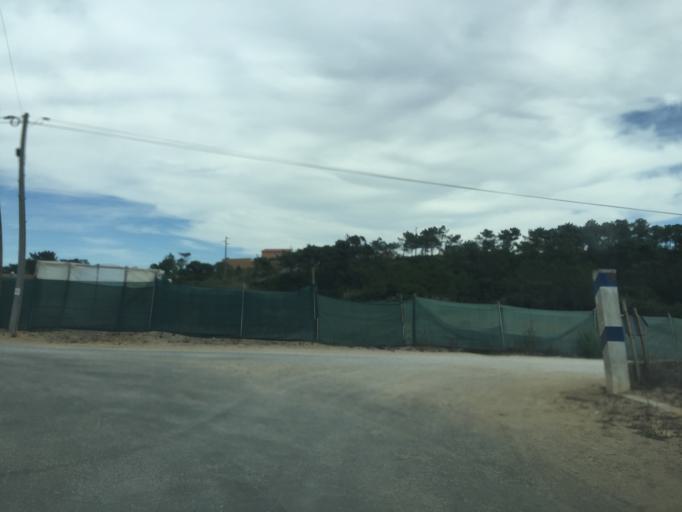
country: PT
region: Lisbon
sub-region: Lourinha
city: Lourinha
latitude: 39.1854
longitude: -9.3403
